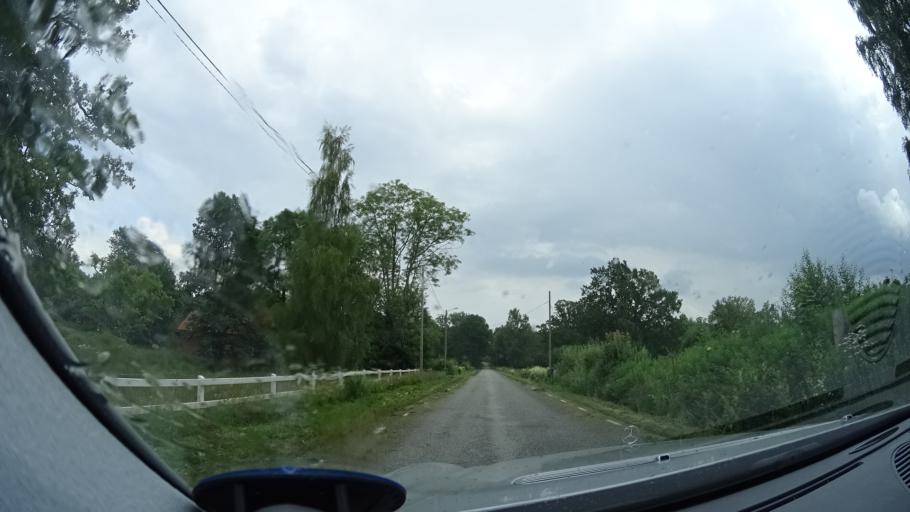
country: SE
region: Kalmar
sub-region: Emmaboda Kommun
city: Emmaboda
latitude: 56.6570
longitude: 15.7023
